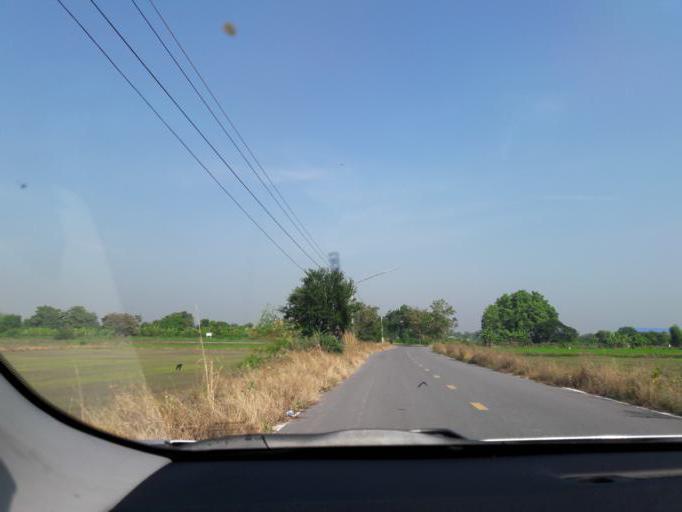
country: TH
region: Ang Thong
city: Ang Thong
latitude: 14.5909
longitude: 100.4297
